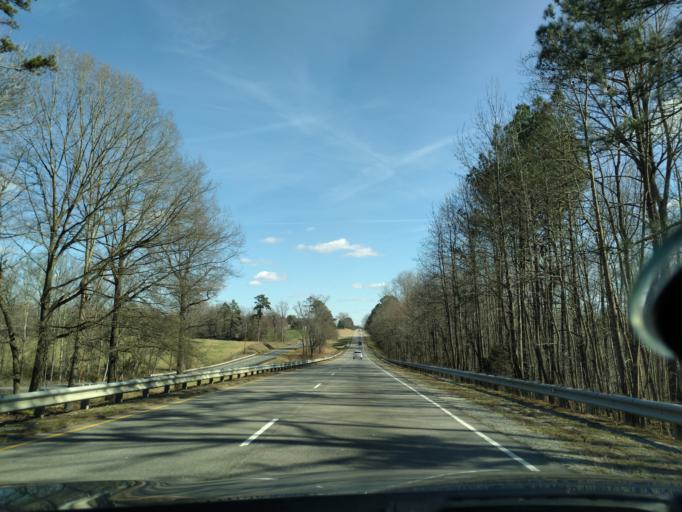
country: US
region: Virginia
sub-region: Nottoway County
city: Crewe
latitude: 37.1899
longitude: -78.1687
